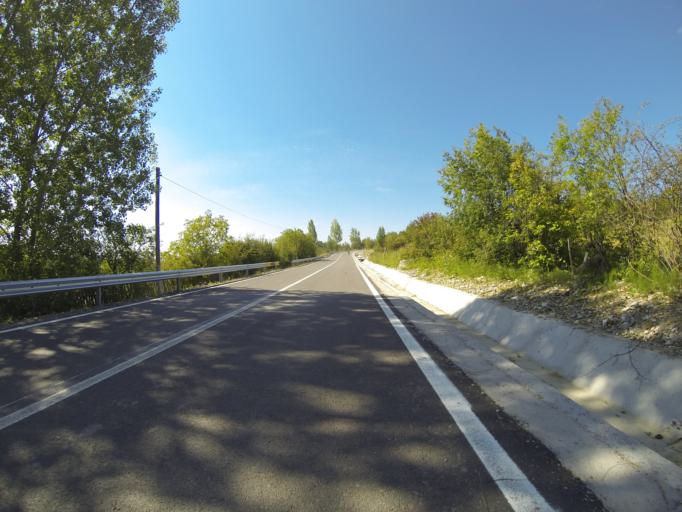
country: RO
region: Gorj
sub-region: Comuna Polovragi
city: Polovragi
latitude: 45.1738
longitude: 23.8503
